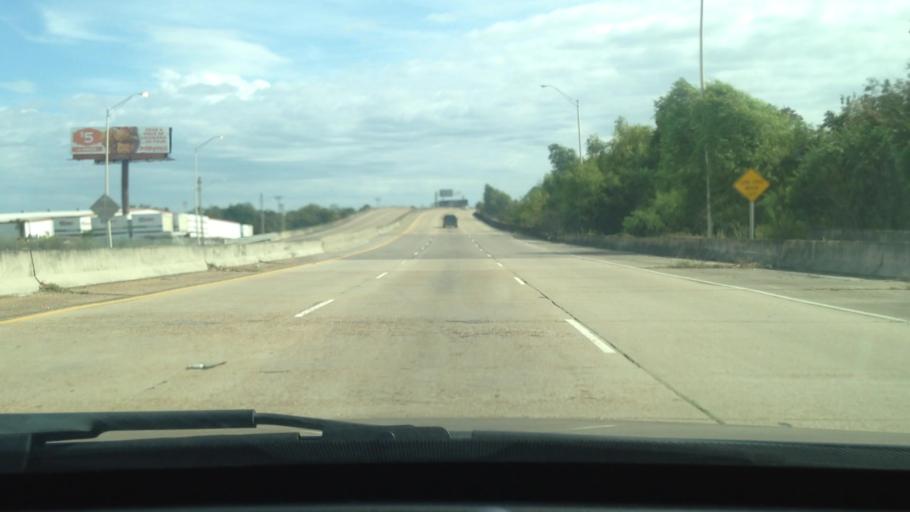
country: US
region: Louisiana
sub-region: Jefferson Parish
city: Jefferson
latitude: 29.9693
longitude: -90.1360
